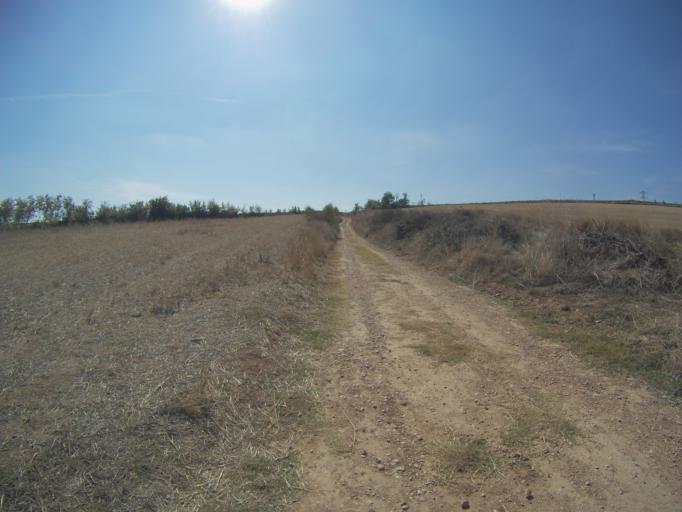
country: ES
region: Navarre
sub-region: Provincia de Navarra
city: Sansol
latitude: 42.5587
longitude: -2.2481
